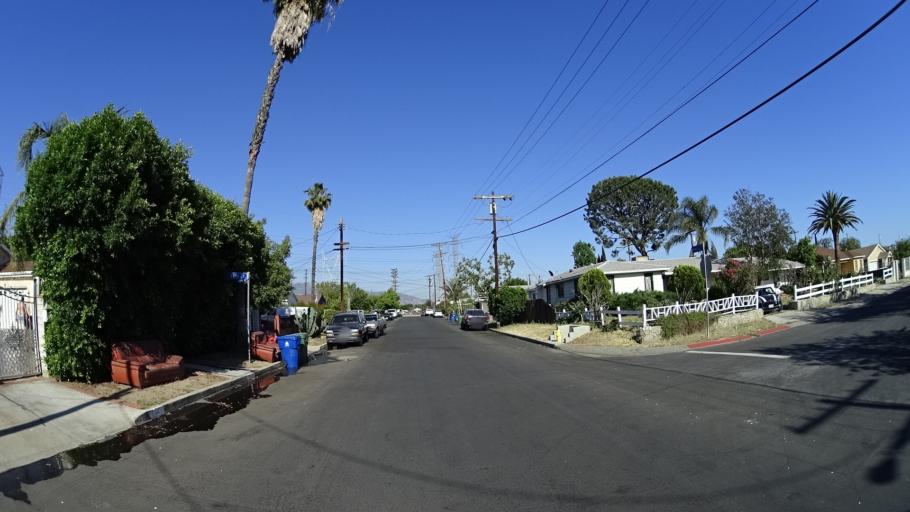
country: US
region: California
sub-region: Los Angeles County
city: North Hollywood
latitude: 34.1831
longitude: -118.3722
